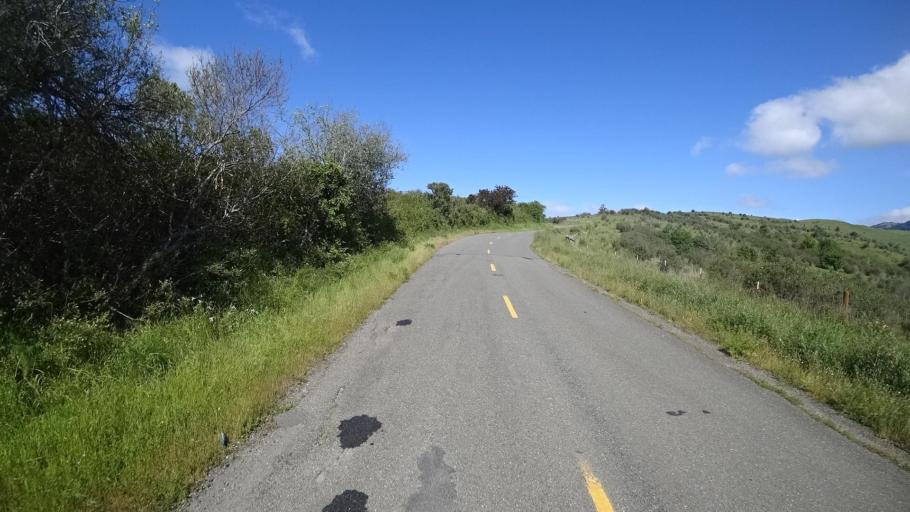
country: US
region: California
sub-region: Humboldt County
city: Ferndale
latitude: 40.3281
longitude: -124.2988
